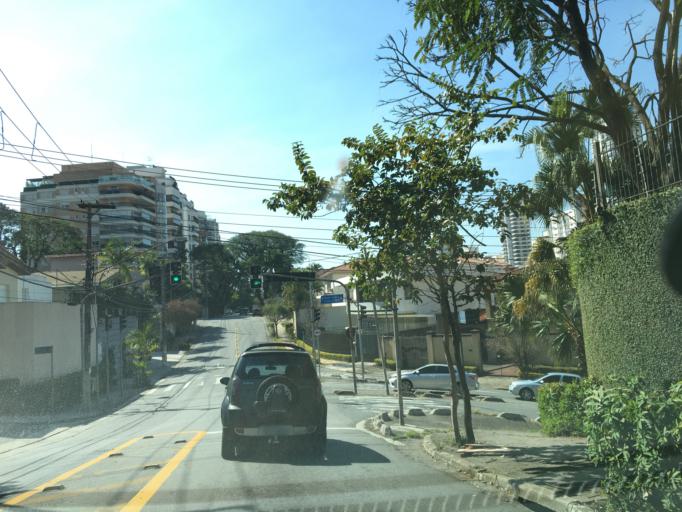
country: BR
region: Sao Paulo
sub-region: Sao Paulo
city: Sao Paulo
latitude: -23.5385
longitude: -46.6653
